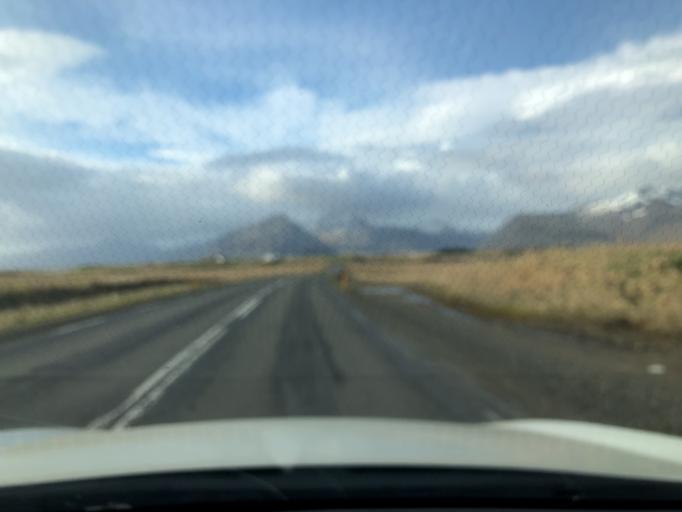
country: IS
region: East
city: Hoefn
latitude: 64.2696
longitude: -15.2024
